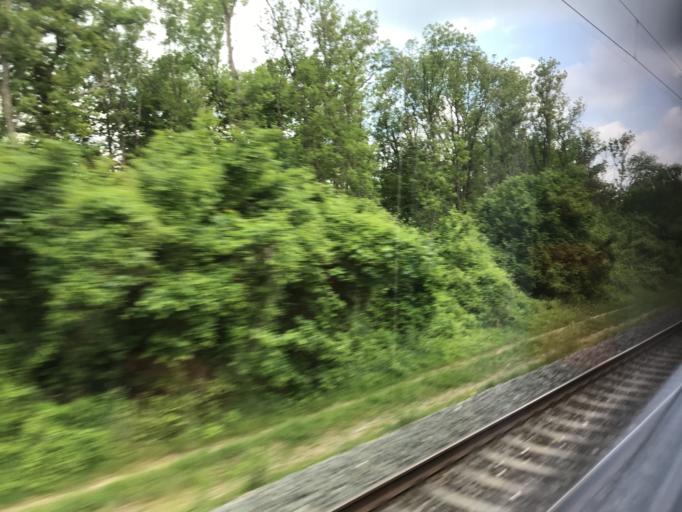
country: DE
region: Bavaria
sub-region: Swabia
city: Leipheim
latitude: 48.4448
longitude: 10.2042
